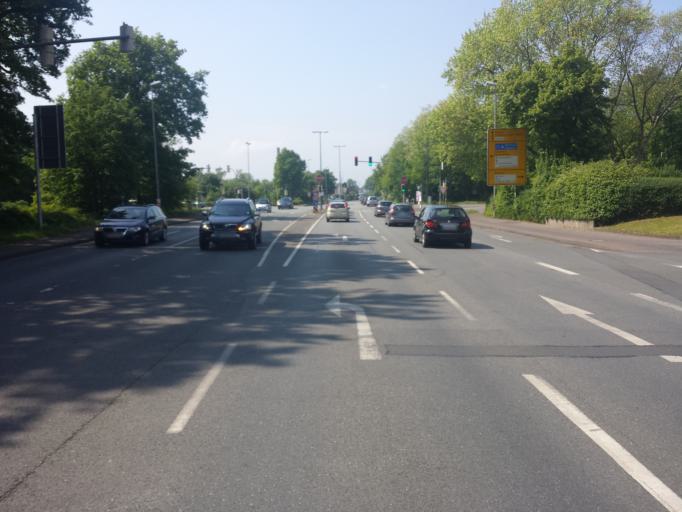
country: DE
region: North Rhine-Westphalia
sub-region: Regierungsbezirk Detmold
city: Guetersloh
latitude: 51.9057
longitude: 8.4074
